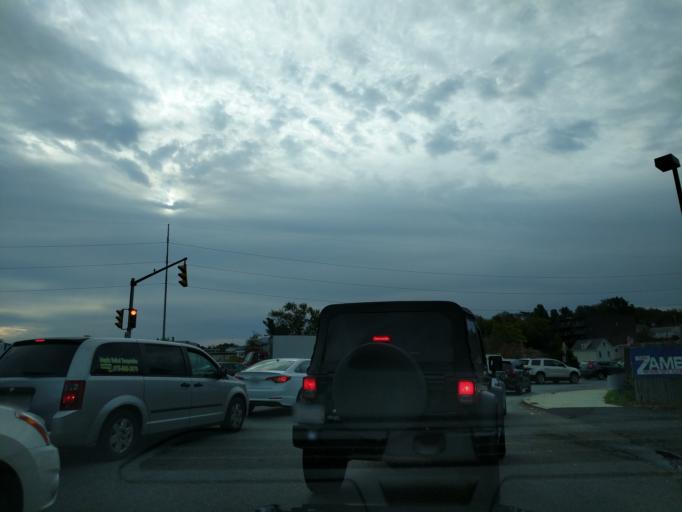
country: US
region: Massachusetts
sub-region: Suffolk County
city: Revere
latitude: 42.4088
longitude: -71.0021
